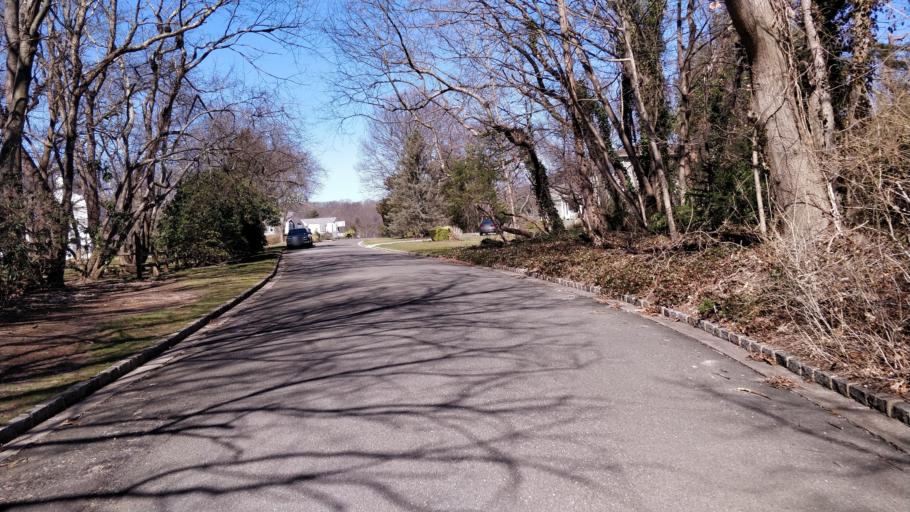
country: US
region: New York
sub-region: Nassau County
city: Syosset
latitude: 40.8331
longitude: -73.5136
